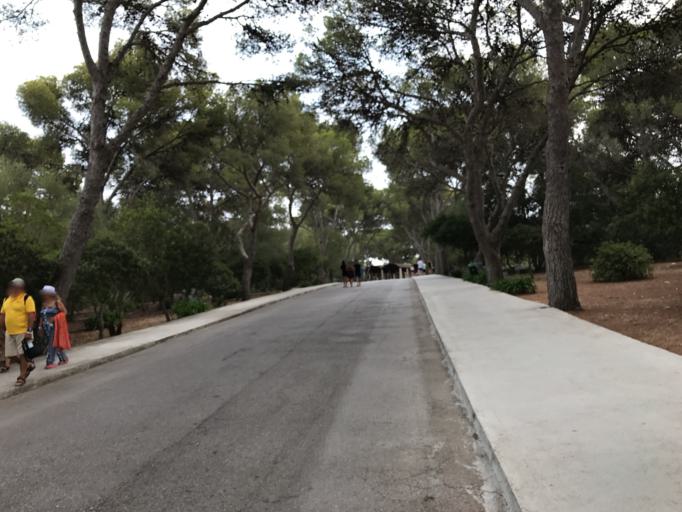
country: ES
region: Balearic Islands
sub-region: Illes Balears
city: Sant Llorenc des Cardassar
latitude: 39.5348
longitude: 3.3306
